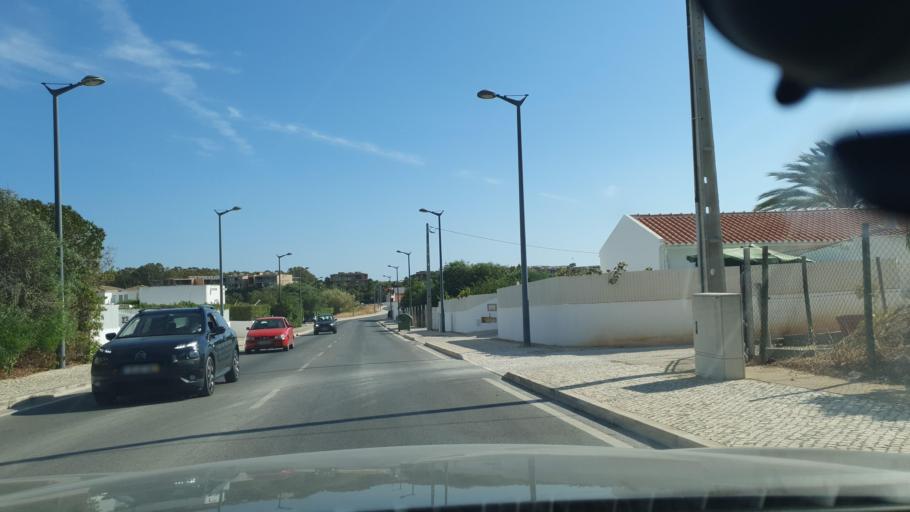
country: PT
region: Faro
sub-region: Albufeira
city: Guia
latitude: 37.0979
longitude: -8.3178
